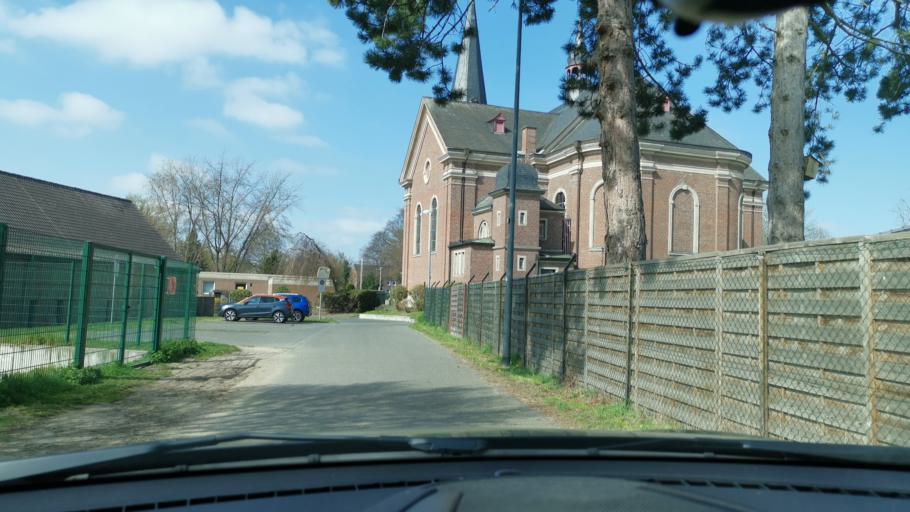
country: DE
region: North Rhine-Westphalia
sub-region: Regierungsbezirk Dusseldorf
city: Grevenbroich
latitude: 51.0907
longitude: 6.5697
